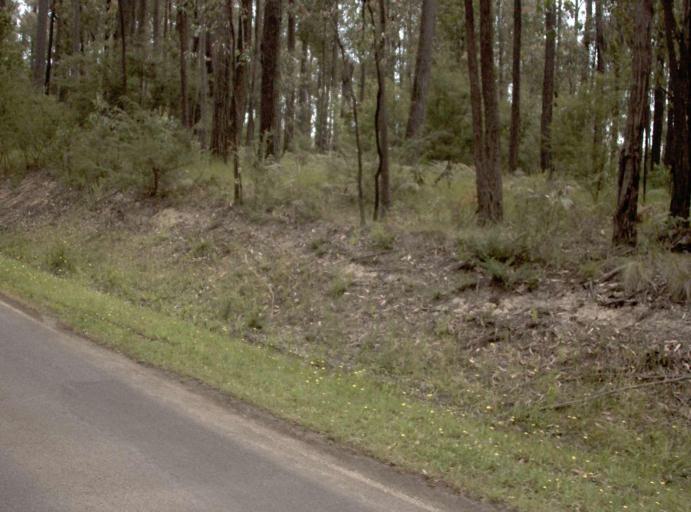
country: AU
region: Victoria
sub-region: Latrobe
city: Traralgon
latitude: -38.0875
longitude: 146.4373
